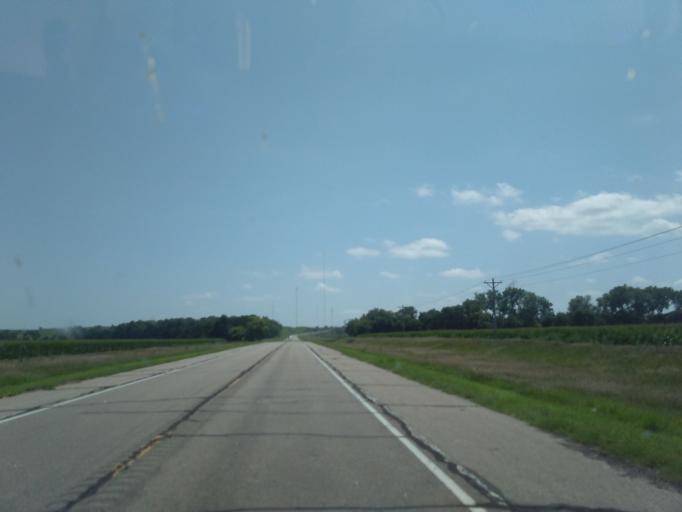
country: US
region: Nebraska
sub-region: Dawson County
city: Lexington
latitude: 40.7175
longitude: -99.7874
